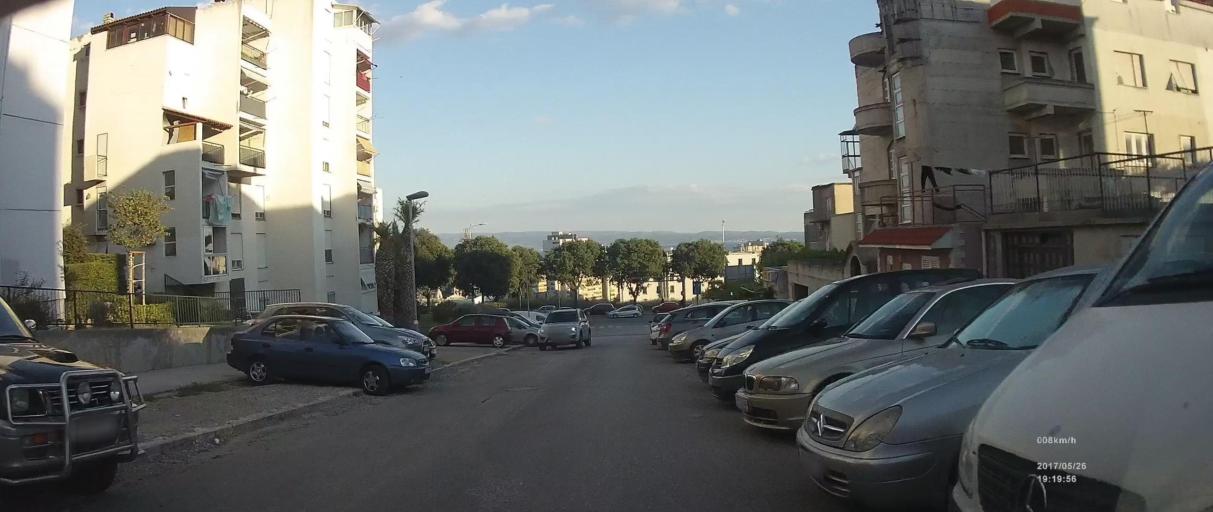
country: HR
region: Splitsko-Dalmatinska
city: Vranjic
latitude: 43.5141
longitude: 16.4658
